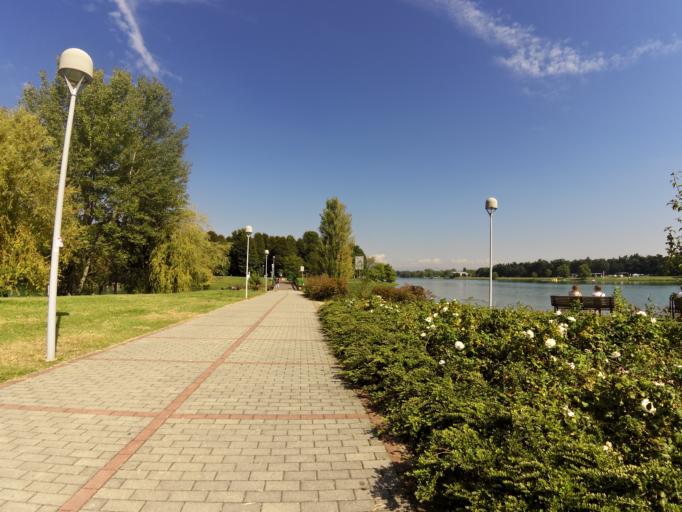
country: IT
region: Lombardy
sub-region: Citta metropolitana di Milano
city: Novegro-Tregarezzo-San Felice
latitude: 45.4617
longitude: 9.2863
